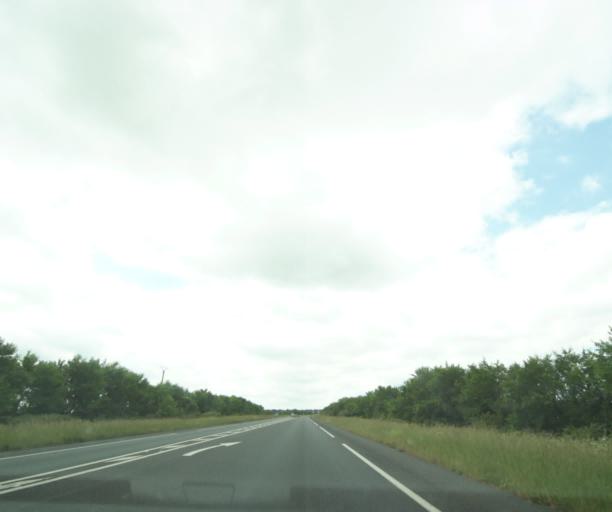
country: FR
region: Poitou-Charentes
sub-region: Departement des Deux-Sevres
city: Saint-Varent
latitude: 46.8787
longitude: -0.1960
